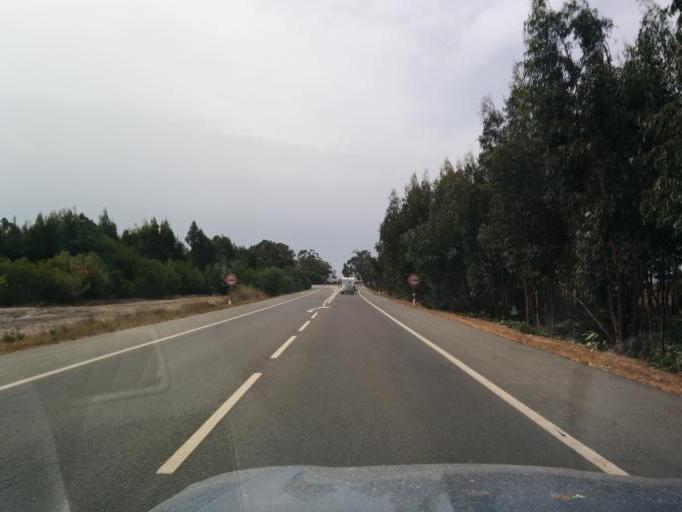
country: PT
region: Beja
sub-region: Odemira
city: Vila Nova de Milfontes
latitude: 37.7062
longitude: -8.7698
